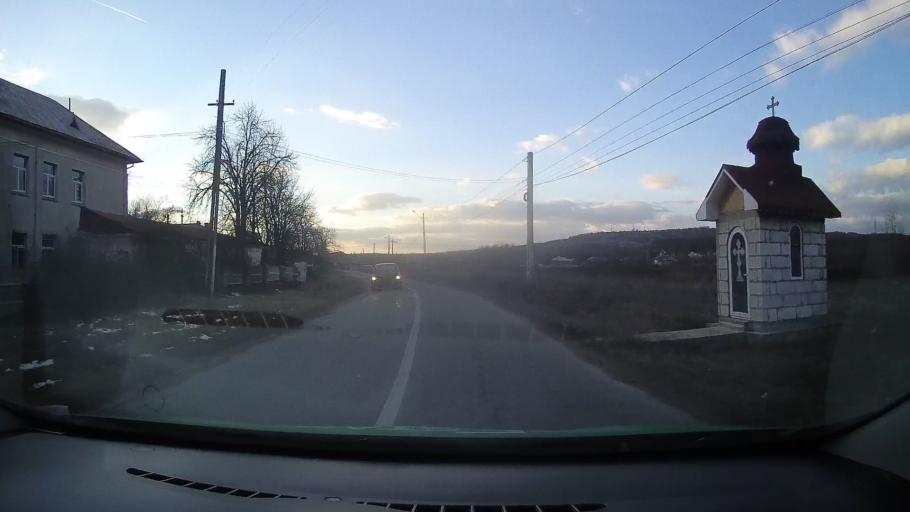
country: RO
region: Dambovita
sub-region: Comuna Gura Ocnitei
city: Gura Ocnitei
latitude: 44.9383
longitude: 25.5822
